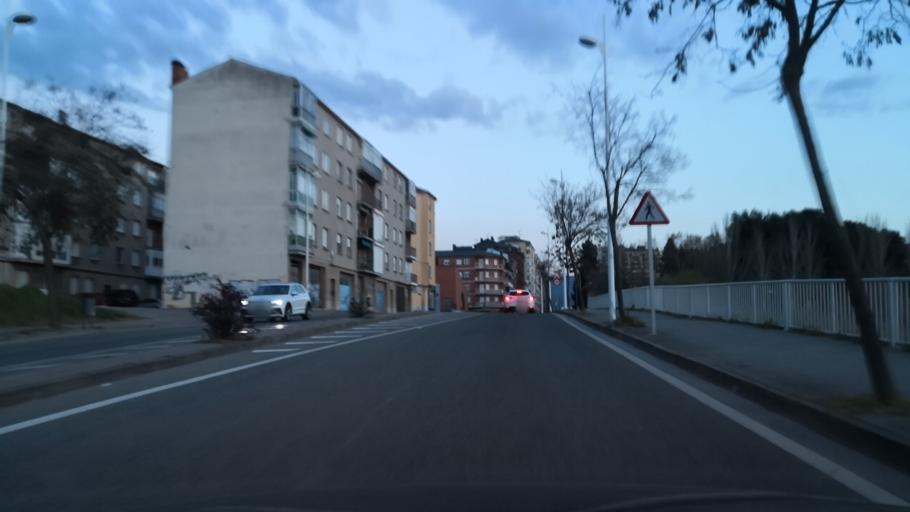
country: ES
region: Castille and Leon
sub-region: Provincia de Leon
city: Ponferrada
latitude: 42.5528
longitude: -6.5854
